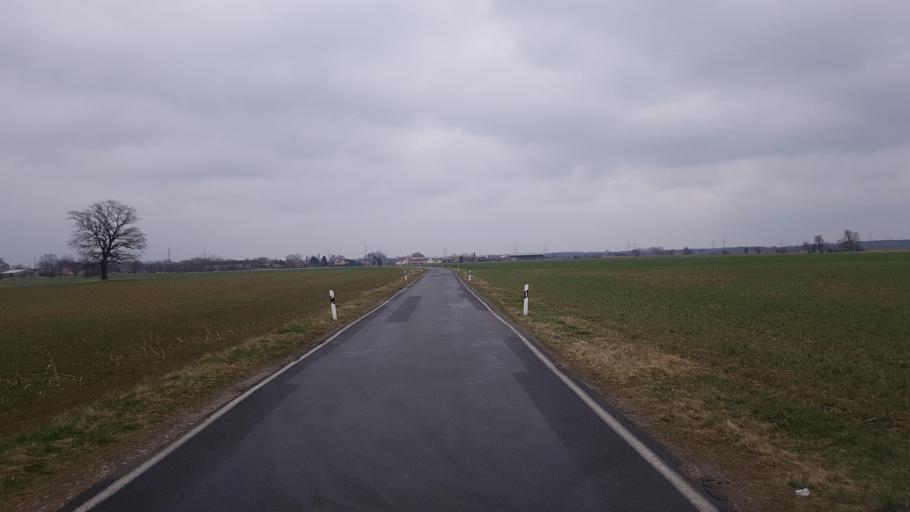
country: DE
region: Saxony
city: Nauwalde
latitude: 51.4248
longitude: 13.3749
